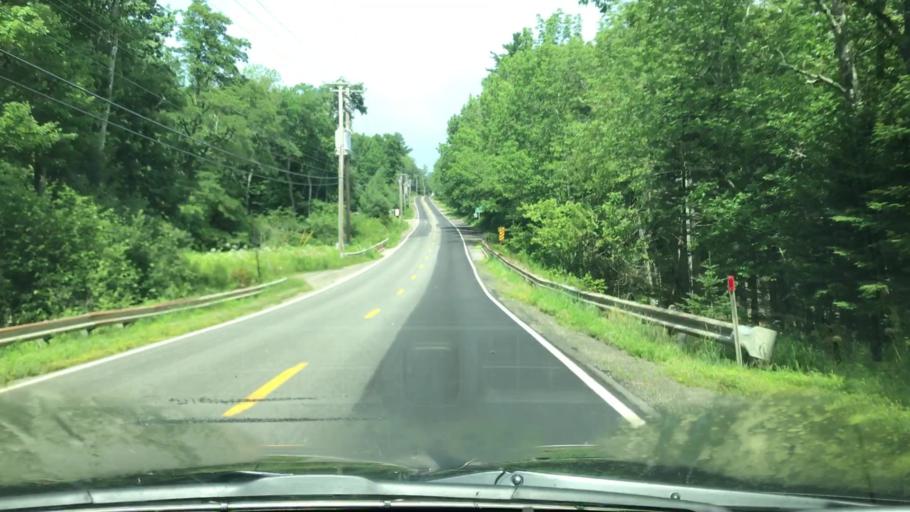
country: US
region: Maine
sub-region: Waldo County
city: Lincolnville
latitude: 44.2500
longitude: -69.0329
